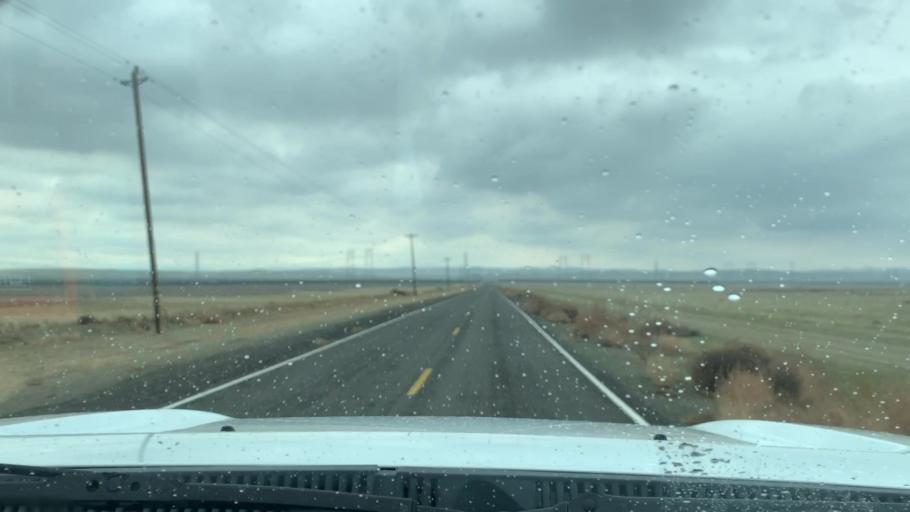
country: US
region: California
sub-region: Kings County
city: Kettleman City
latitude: 35.9344
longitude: -119.8901
